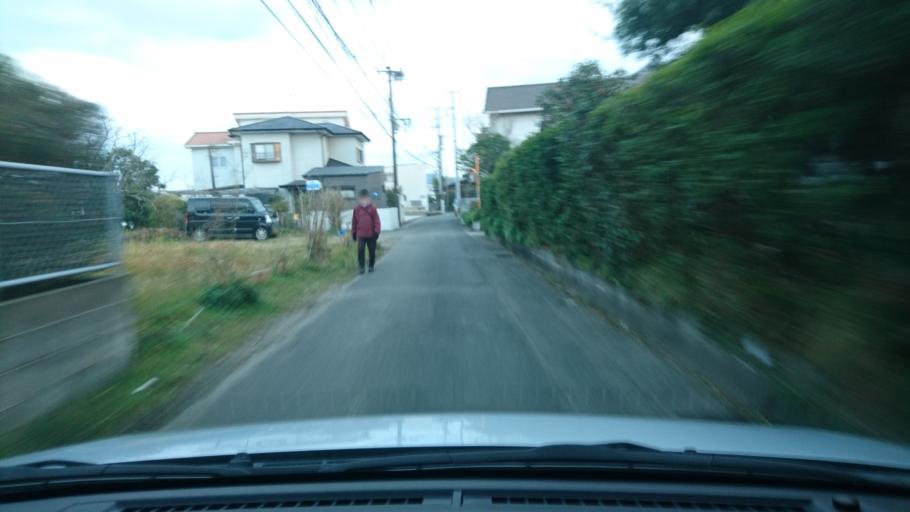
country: JP
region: Miyazaki
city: Miyazaki-shi
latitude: 31.8529
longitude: 131.4315
